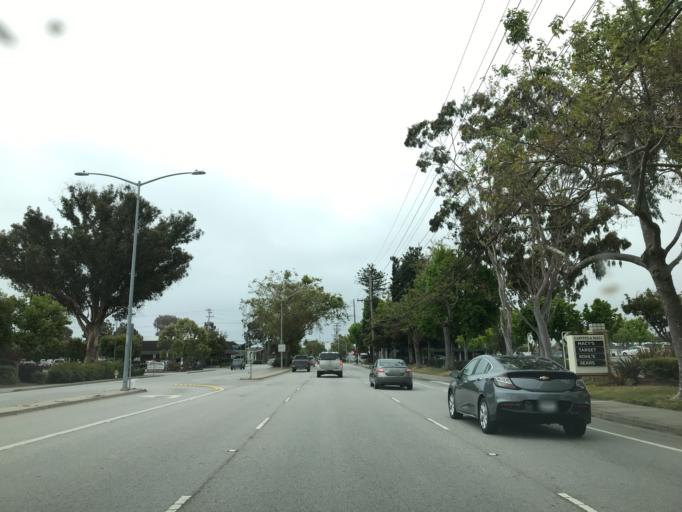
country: US
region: California
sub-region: Santa Cruz County
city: Capitola
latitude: 36.9754
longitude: -121.9651
